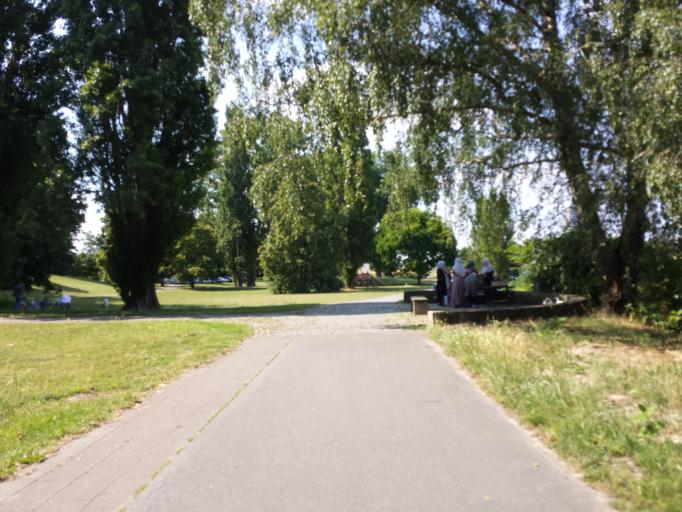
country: DE
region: Bremen
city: Bremen
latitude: 53.0906
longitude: 8.7629
